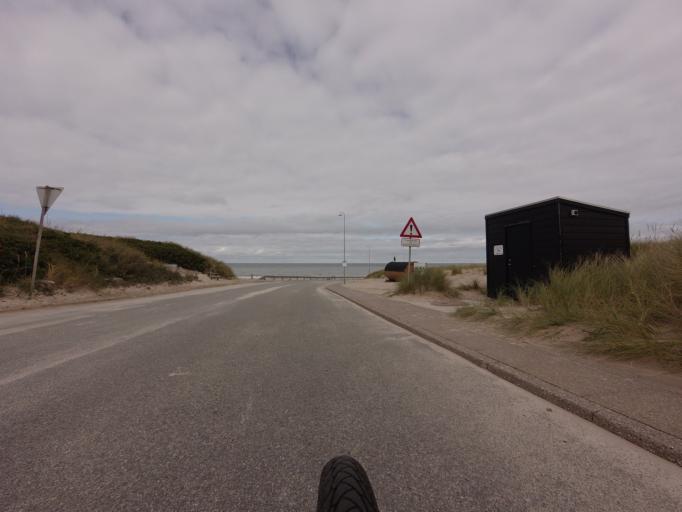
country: DK
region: North Denmark
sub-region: Hjorring Kommune
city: Hirtshals
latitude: 57.5905
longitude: 9.9524
